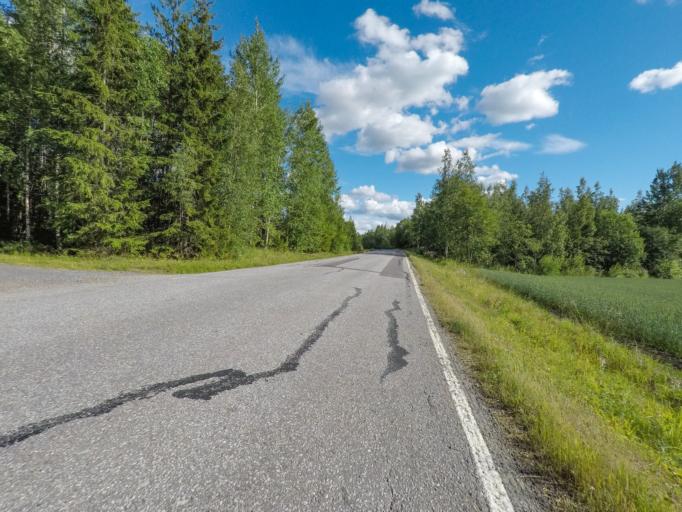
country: FI
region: South Karelia
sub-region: Imatra
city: Imatra
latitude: 61.1326
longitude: 28.6607
